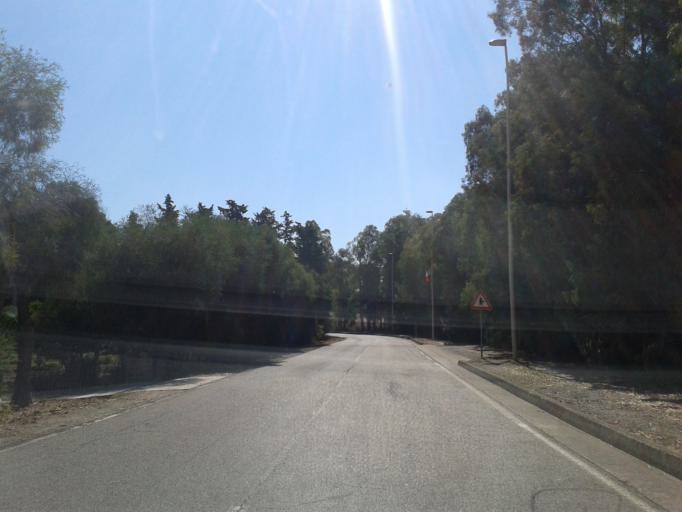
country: IT
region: Sardinia
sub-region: Provincia di Cagliari
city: Castiadas
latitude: 39.2056
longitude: 9.5469
